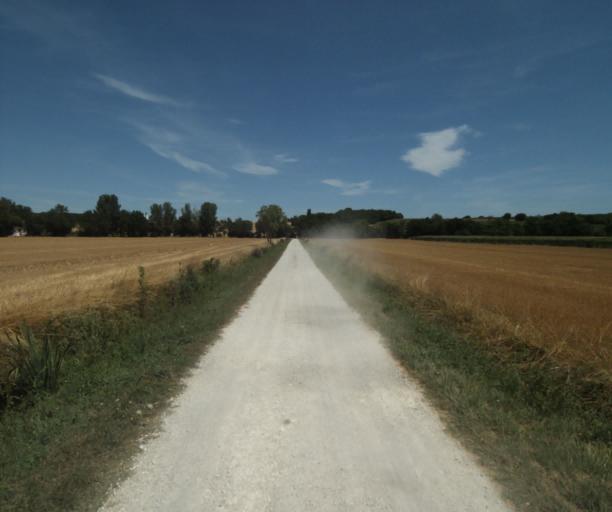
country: FR
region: Midi-Pyrenees
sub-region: Departement de la Haute-Garonne
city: Revel
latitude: 43.4995
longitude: 2.0383
